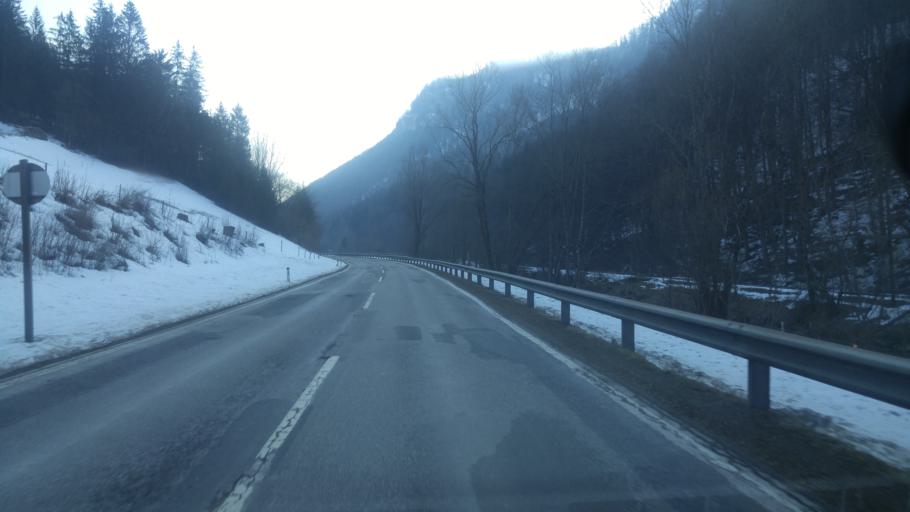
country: AT
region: Lower Austria
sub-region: Politischer Bezirk Lilienfeld
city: Lilienfeld
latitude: 47.9671
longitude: 15.5812
